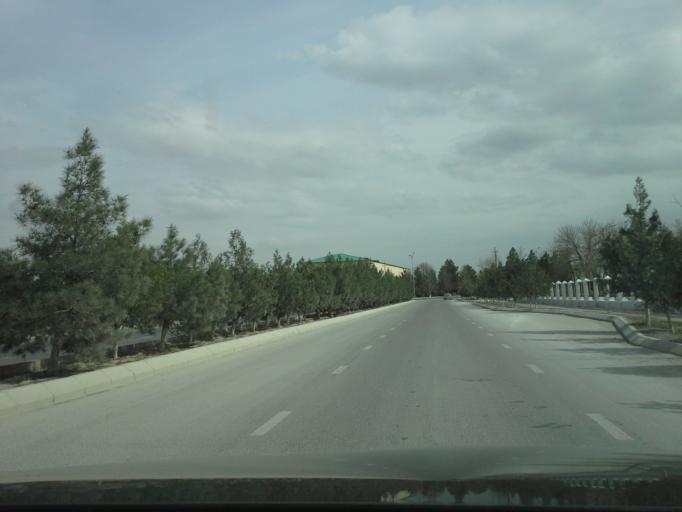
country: TM
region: Ahal
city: Abadan
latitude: 38.0460
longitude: 58.1845
